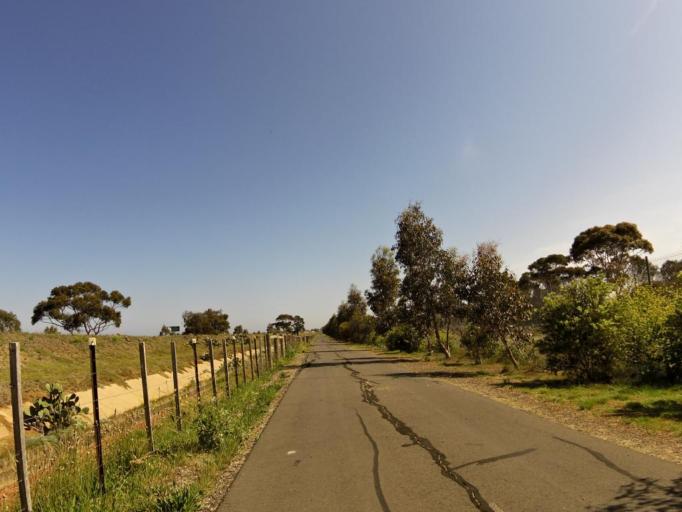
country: AU
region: Victoria
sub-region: Wyndham
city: Hoppers Crossing
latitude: -37.9036
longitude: 144.6985
